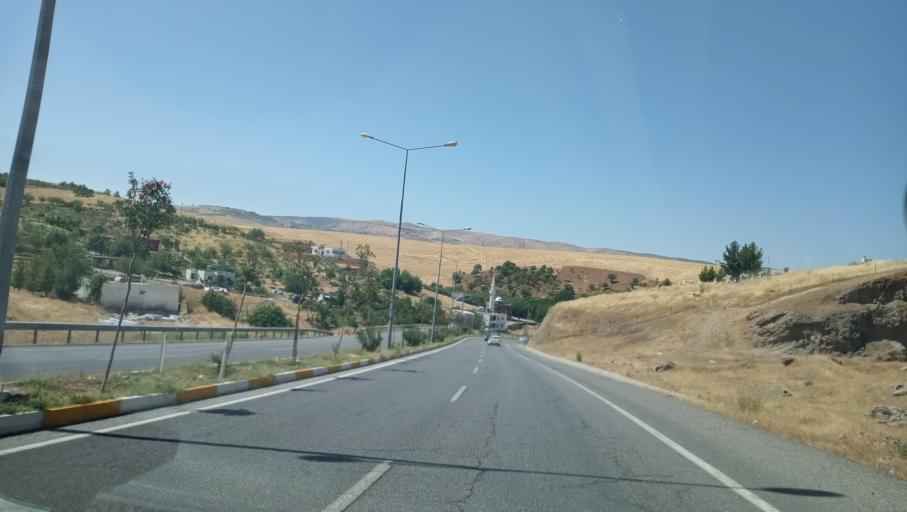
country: TR
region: Siirt
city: Civankan
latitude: 37.9499
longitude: 41.8771
